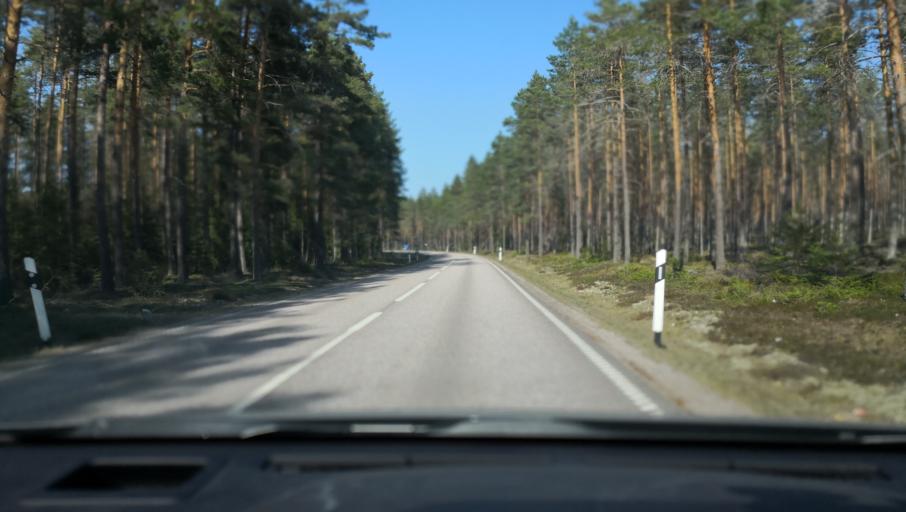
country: SE
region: Uppsala
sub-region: Heby Kommun
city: Tarnsjo
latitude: 60.0710
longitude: 16.8765
